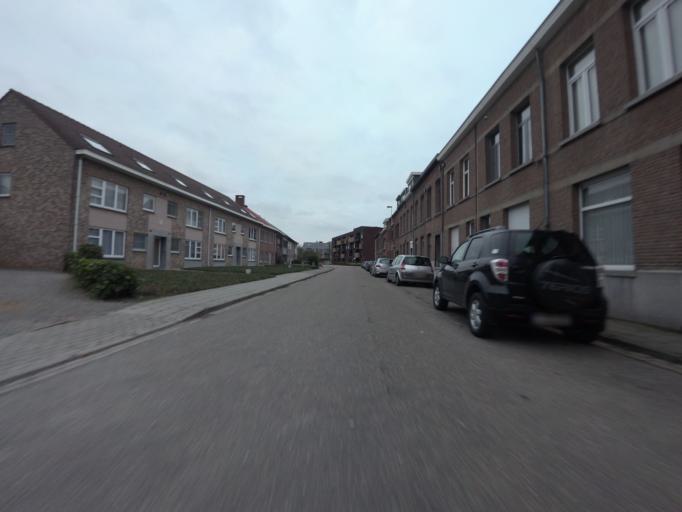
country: BE
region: Flanders
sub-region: Provincie Antwerpen
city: Lier
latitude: 51.1275
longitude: 4.5847
